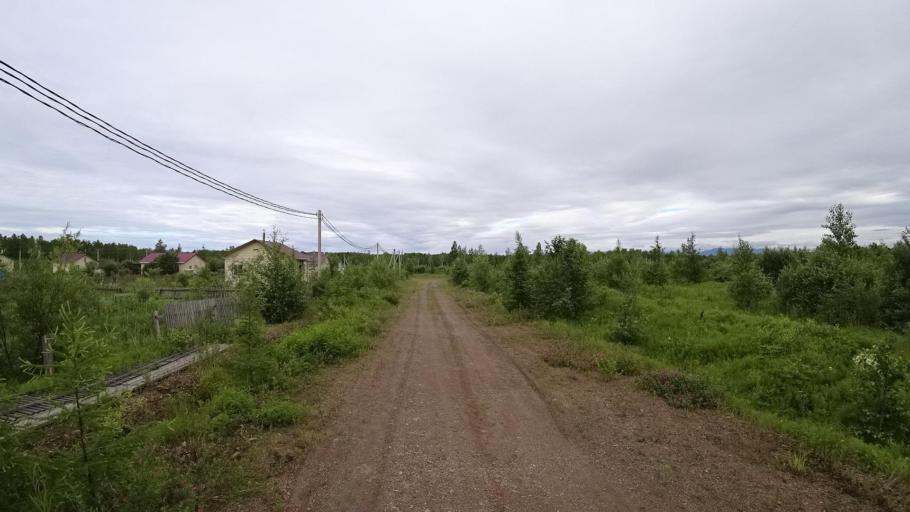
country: RU
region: Khabarovsk Krai
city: Amursk
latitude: 49.8970
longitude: 136.1629
